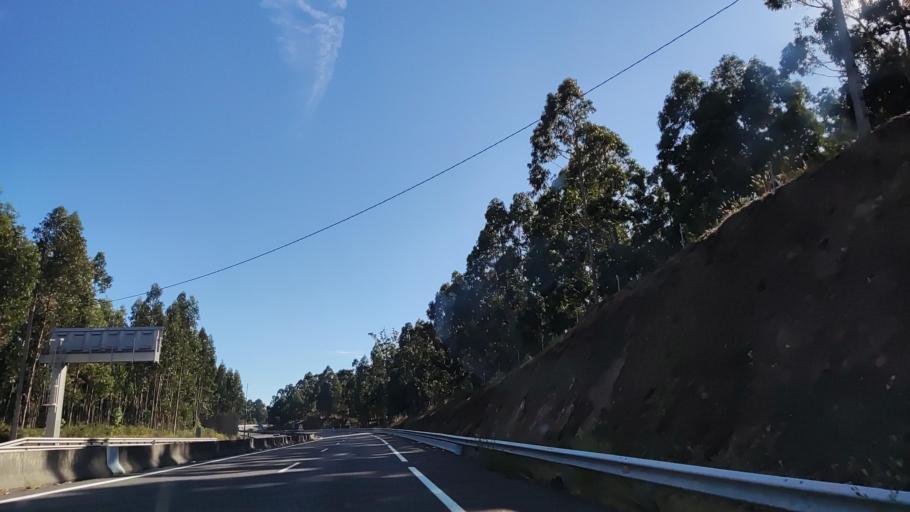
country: ES
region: Galicia
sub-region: Provincia da Coruna
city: Boiro
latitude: 42.5820
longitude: -8.9868
